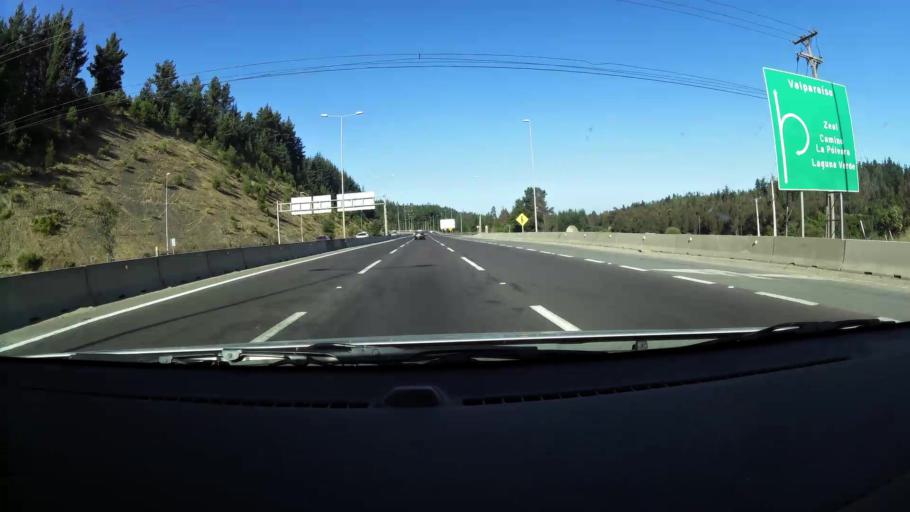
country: CL
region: Valparaiso
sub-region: Provincia de Valparaiso
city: Vina del Mar
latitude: -33.1082
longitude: -71.5540
